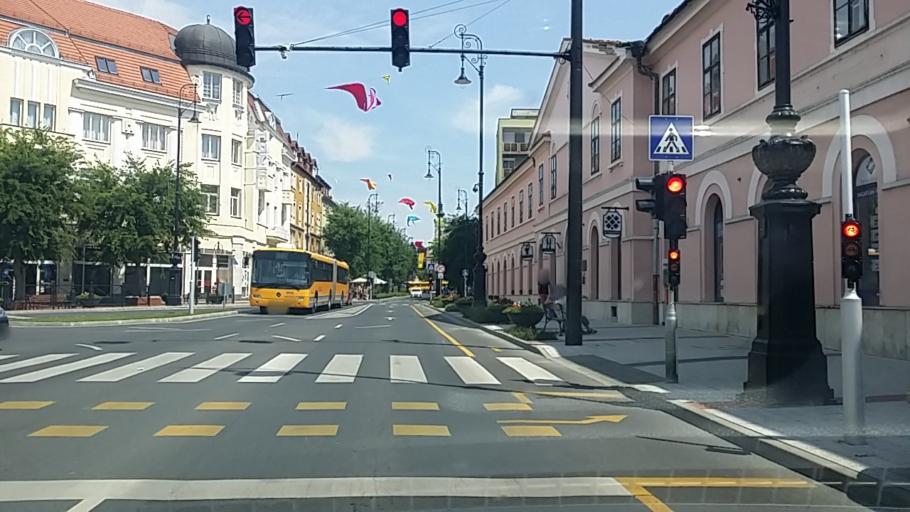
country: HU
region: Zala
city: Nagykanizsa
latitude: 46.4552
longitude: 16.9887
